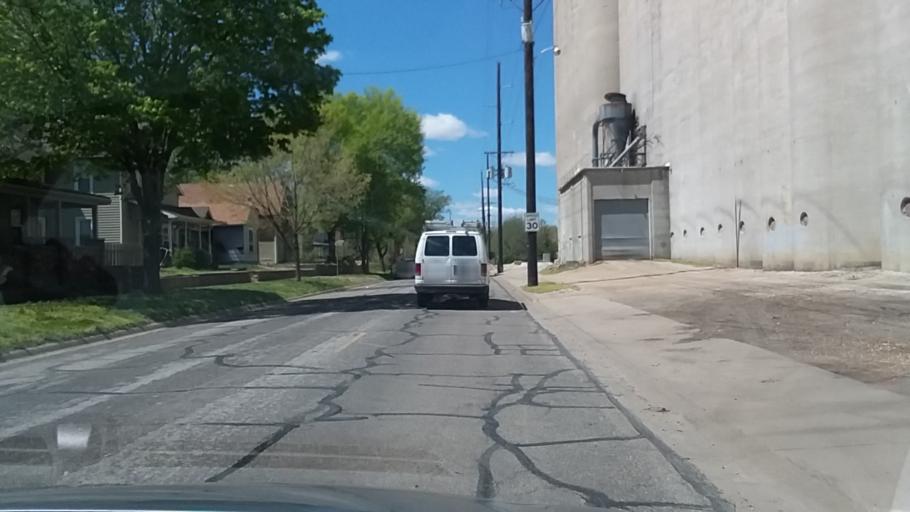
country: US
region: Kansas
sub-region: Douglas County
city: Lawrence
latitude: 38.9778
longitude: -95.2314
